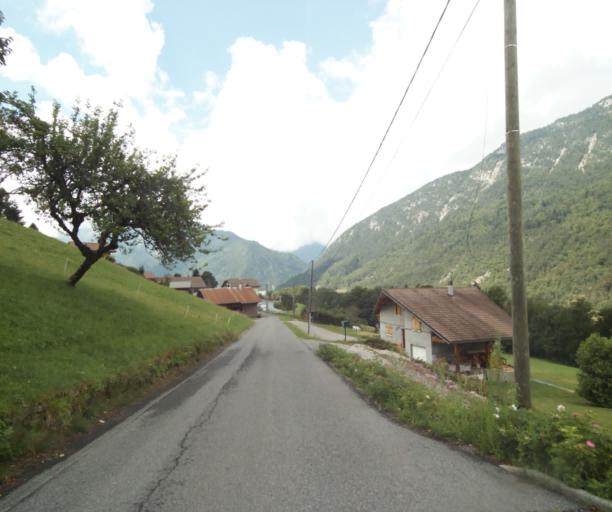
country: FR
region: Rhone-Alpes
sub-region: Departement de la Haute-Savoie
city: Thones
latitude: 45.8942
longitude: 6.3440
